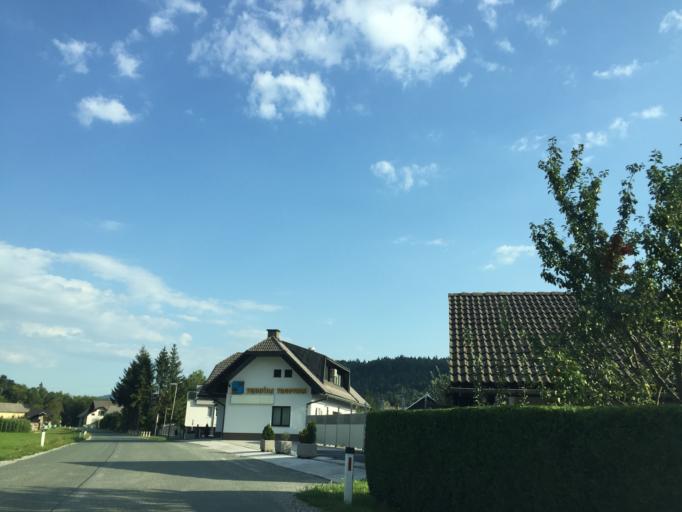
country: SI
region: Trzic
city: Bistrica pri Trzicu
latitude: 46.3116
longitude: 14.2400
